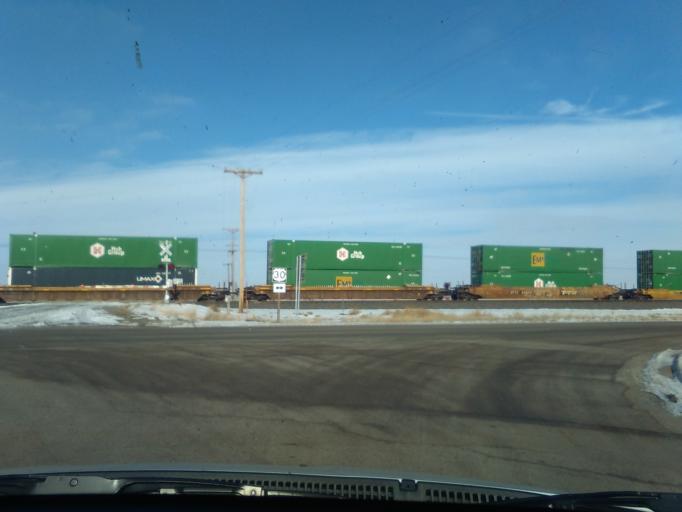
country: US
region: Wyoming
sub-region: Laramie County
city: Pine Bluffs
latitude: 41.1870
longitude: -104.0457
